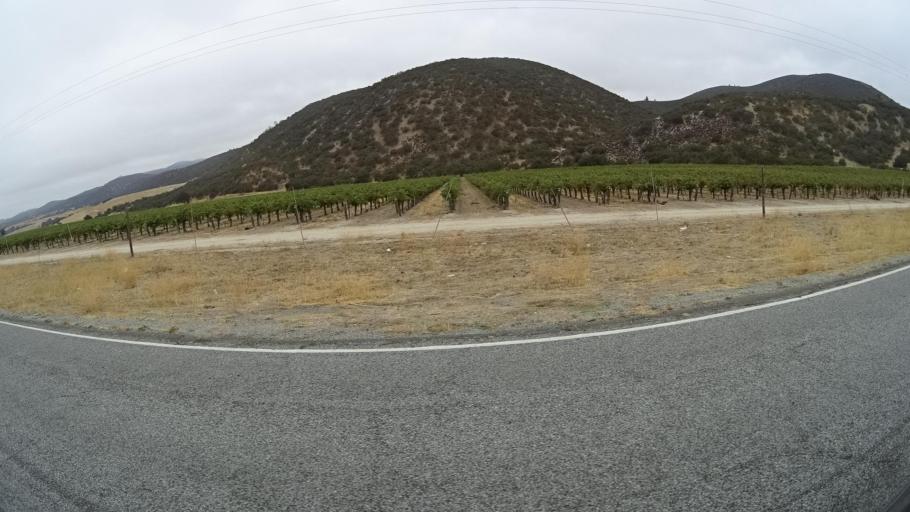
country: US
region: California
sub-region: San Luis Obispo County
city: Lake Nacimiento
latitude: 35.8870
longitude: -120.9178
